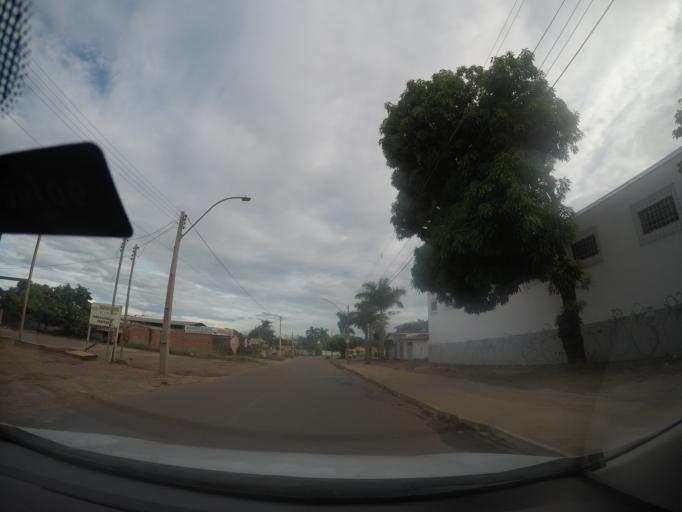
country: BR
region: Goias
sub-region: Goiania
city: Goiania
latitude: -16.6549
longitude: -49.3188
